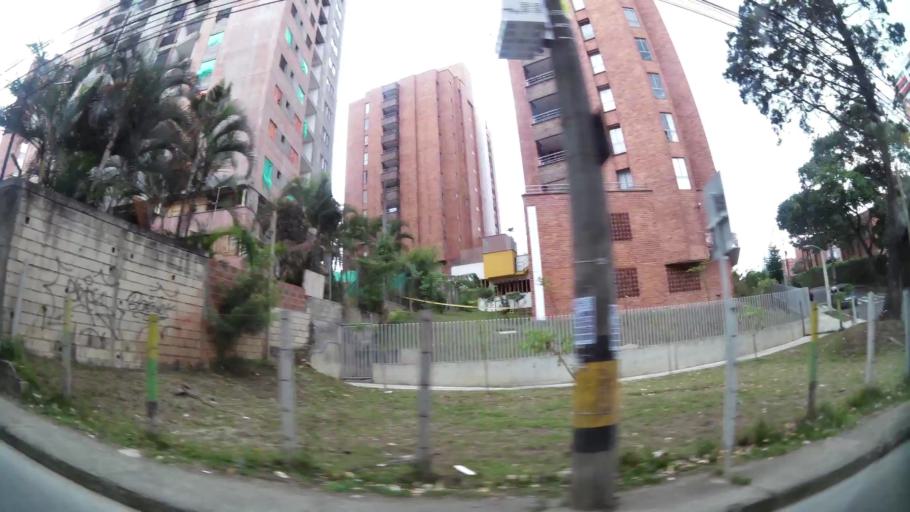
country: CO
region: Antioquia
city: Medellin
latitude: 6.2757
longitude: -75.5848
